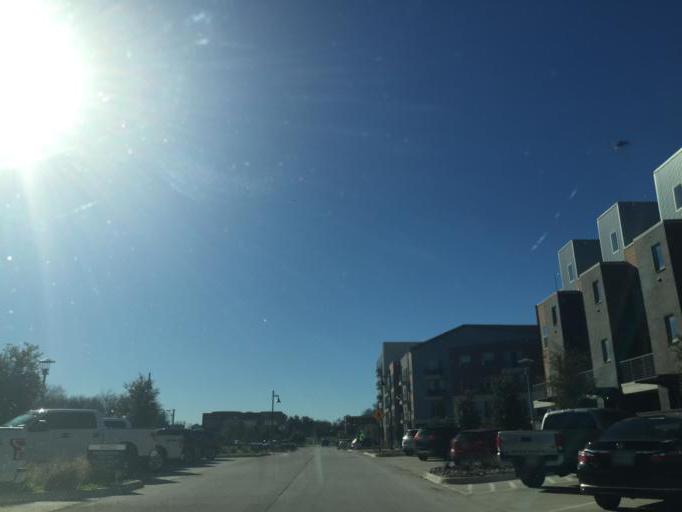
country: US
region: Texas
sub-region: Tarrant County
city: Fort Worth
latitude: 32.7536
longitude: -97.3490
